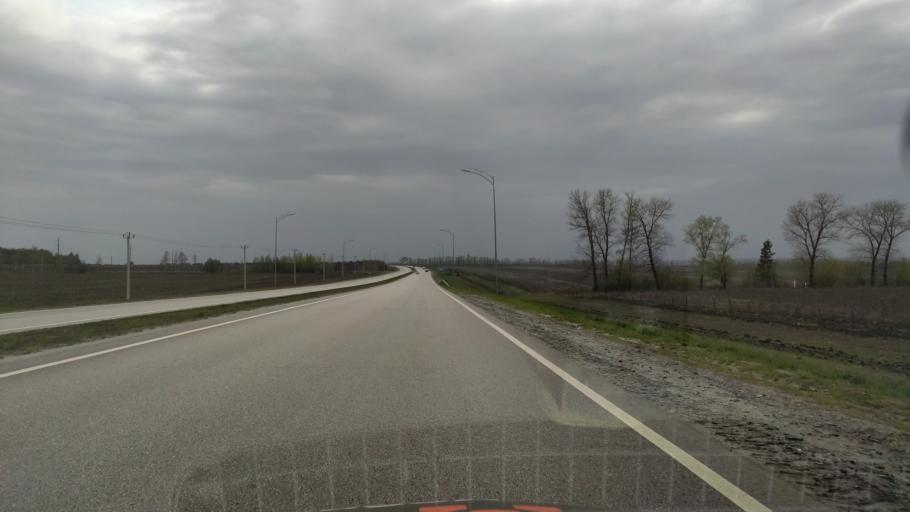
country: RU
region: Belgorod
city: Staryy Oskol
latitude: 51.3846
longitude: 37.8586
